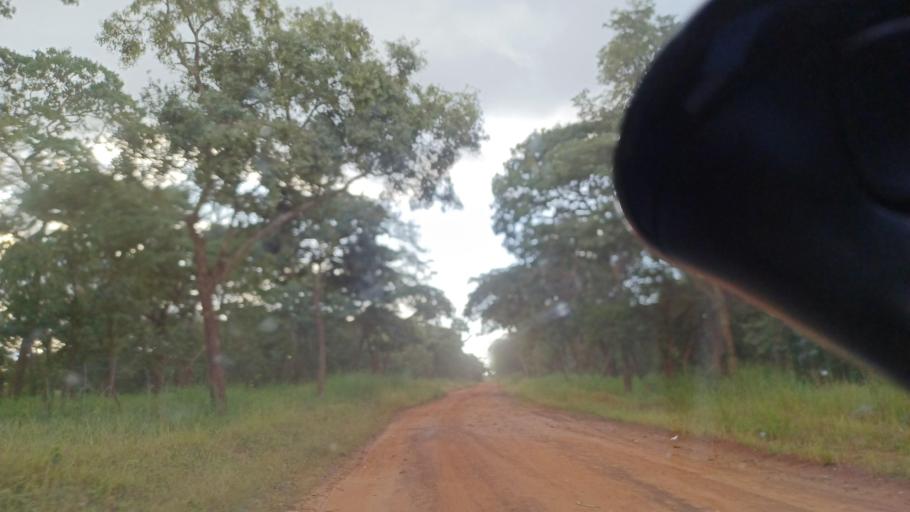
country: ZM
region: North-Western
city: Kasempa
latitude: -13.5406
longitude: 25.9881
